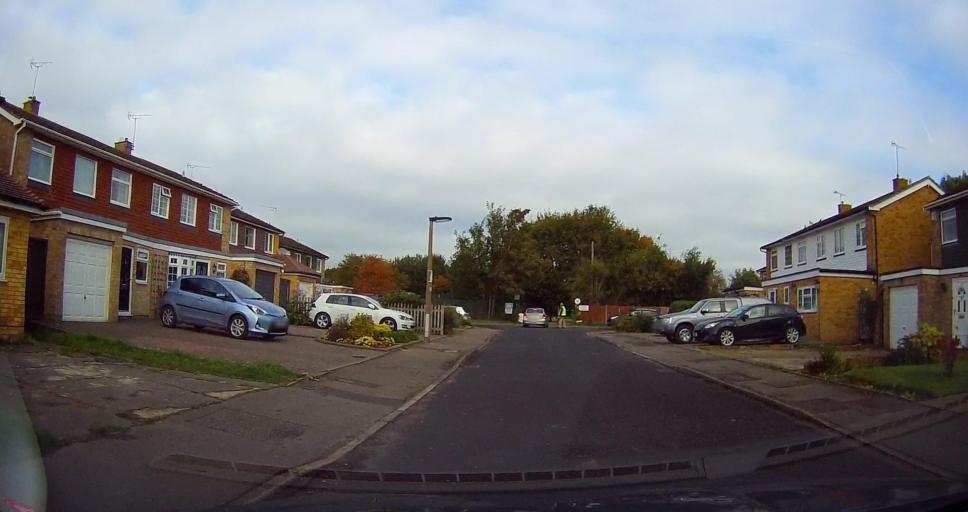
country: GB
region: England
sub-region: Kent
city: East Peckham
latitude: 51.2146
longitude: 0.3838
